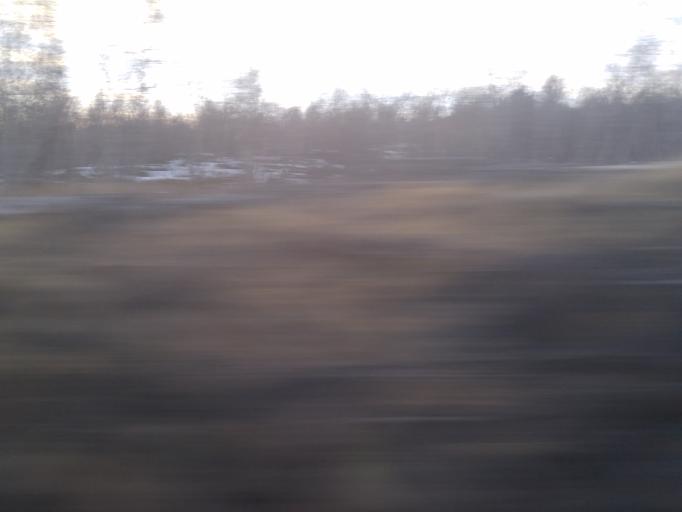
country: NO
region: Oppland
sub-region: Dovre
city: Dovre
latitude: 62.1860
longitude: 9.4745
